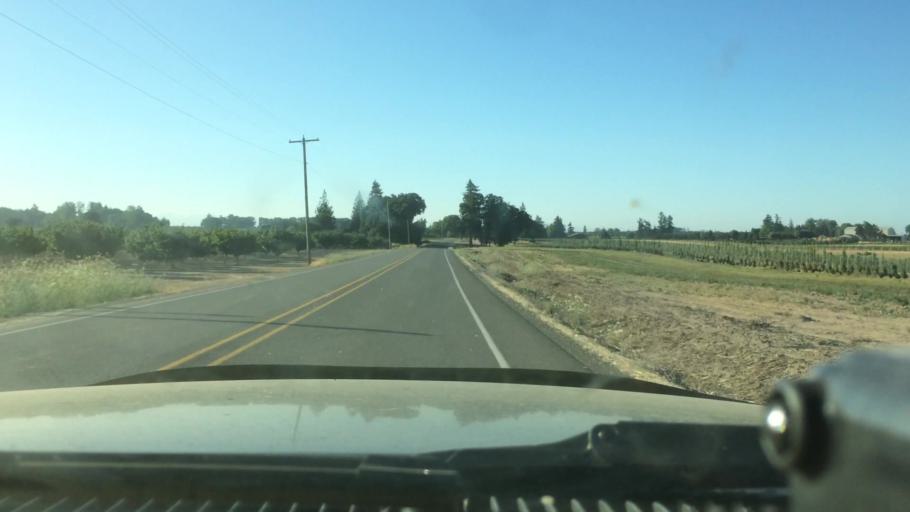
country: US
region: Oregon
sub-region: Marion County
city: Gervais
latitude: 45.1251
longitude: -122.9891
